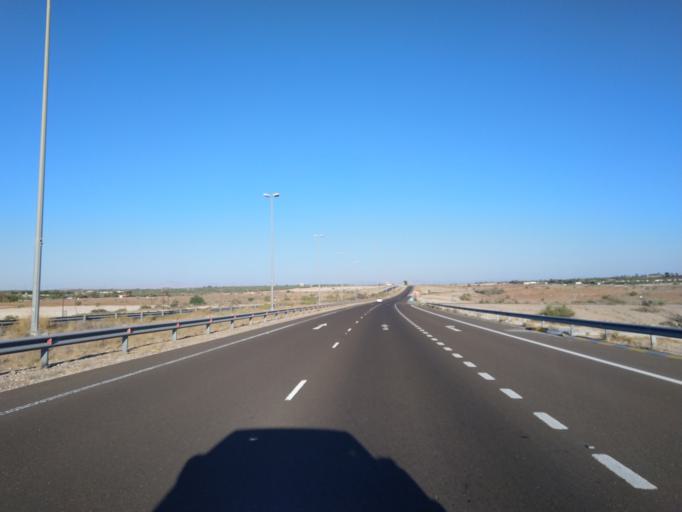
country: OM
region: Al Buraimi
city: Al Buraymi
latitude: 24.5375
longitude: 55.5951
